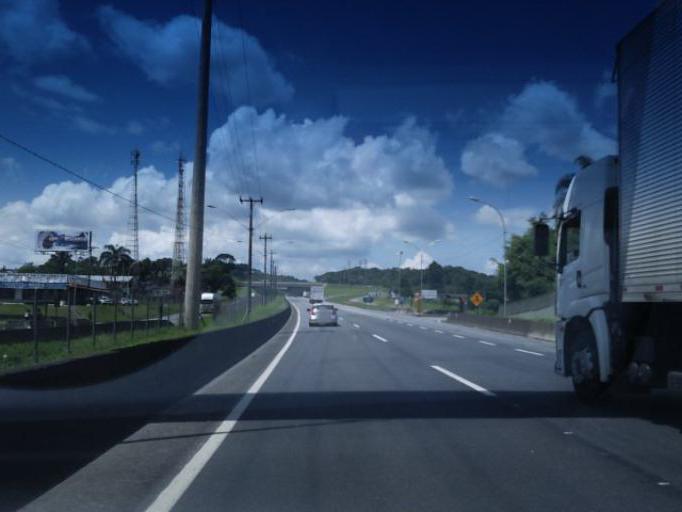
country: BR
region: Sao Paulo
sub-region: Juquitiba
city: Juquitiba
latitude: -23.9221
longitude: -46.9923
